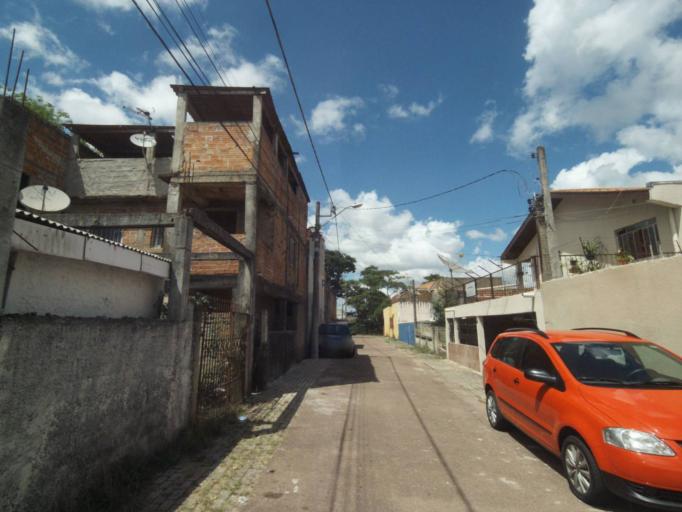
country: BR
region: Parana
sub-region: Curitiba
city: Curitiba
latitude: -25.5042
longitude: -49.3244
